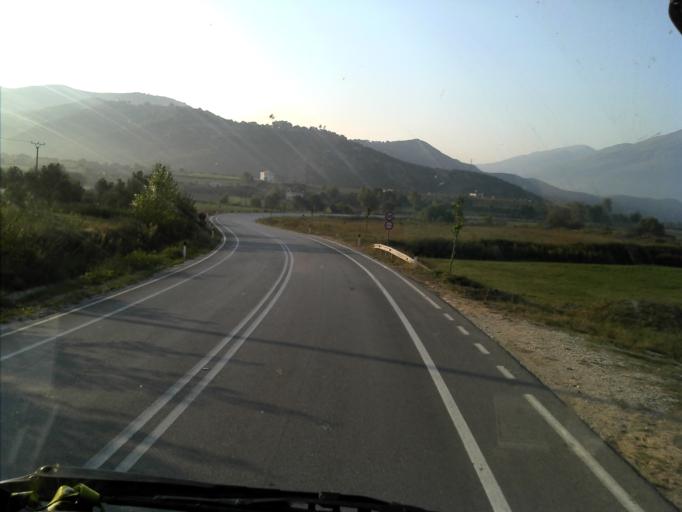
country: AL
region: Gjirokaster
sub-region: Rrethi i Tepelenes
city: Krahes
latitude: 40.4244
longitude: 19.8550
